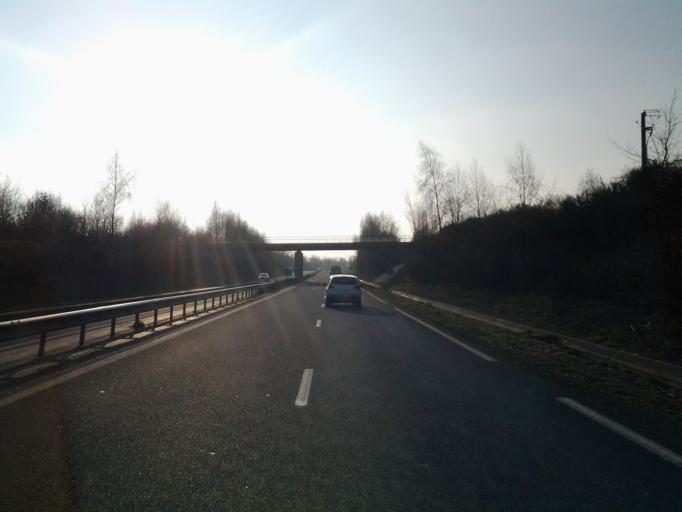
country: FR
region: Pays de la Loire
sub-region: Departement de la Vendee
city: La Roche-sur-Yon
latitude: 46.6790
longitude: -1.3852
